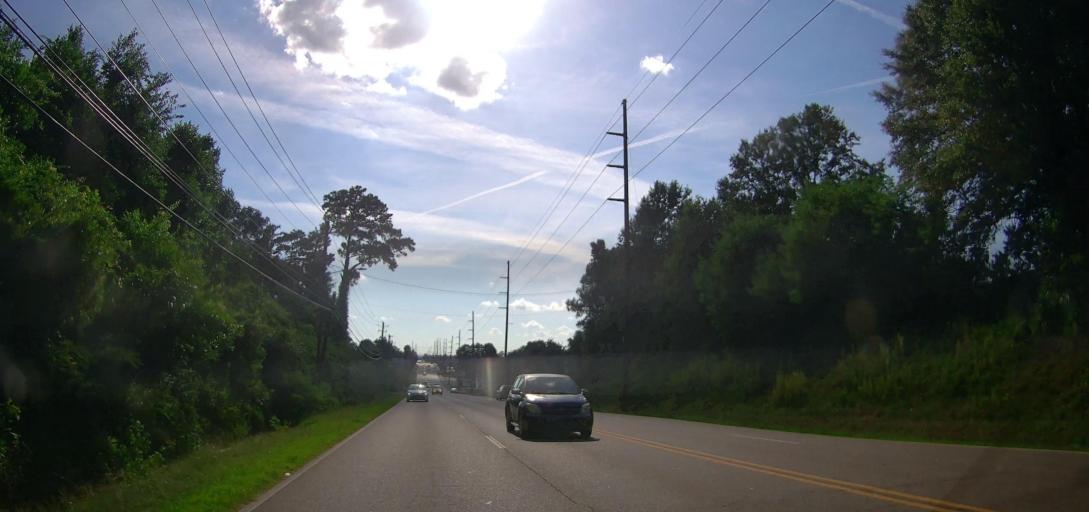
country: US
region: Alabama
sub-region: Tuscaloosa County
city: Holt
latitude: 33.2065
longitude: -87.4942
